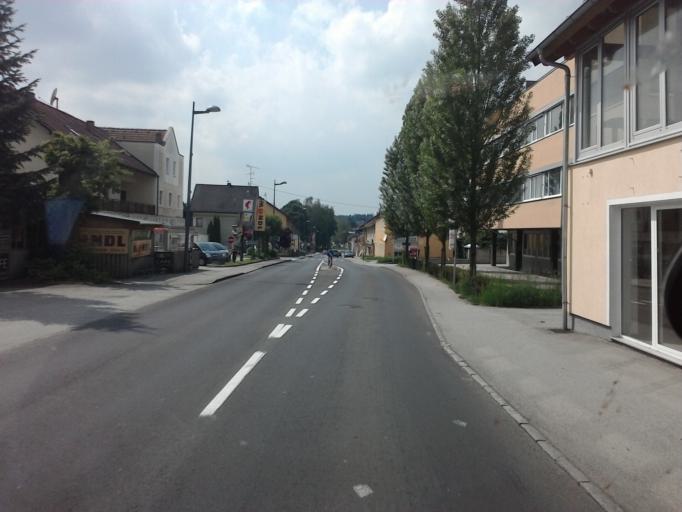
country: AT
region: Upper Austria
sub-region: Wels-Land
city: Sattledt
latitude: 48.0731
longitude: 14.0604
